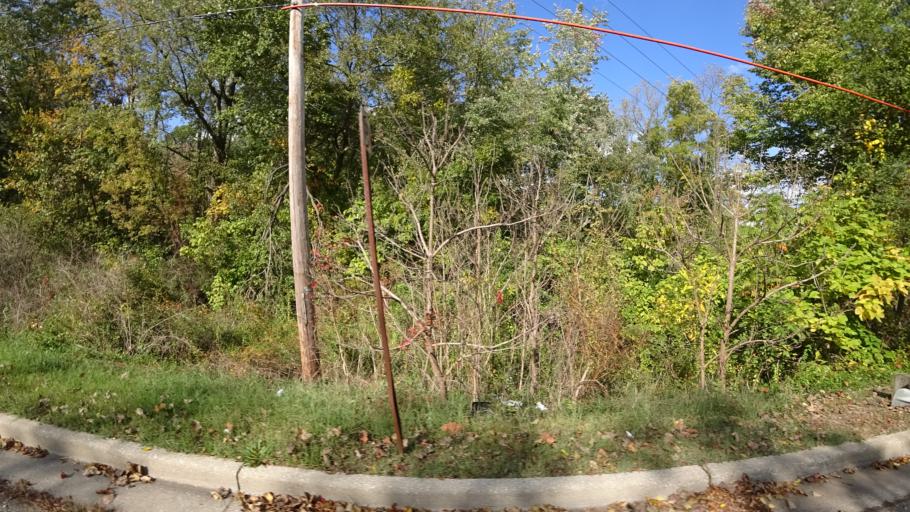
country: US
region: Michigan
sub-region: Saint Joseph County
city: Three Rivers
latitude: 41.9547
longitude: -85.6247
